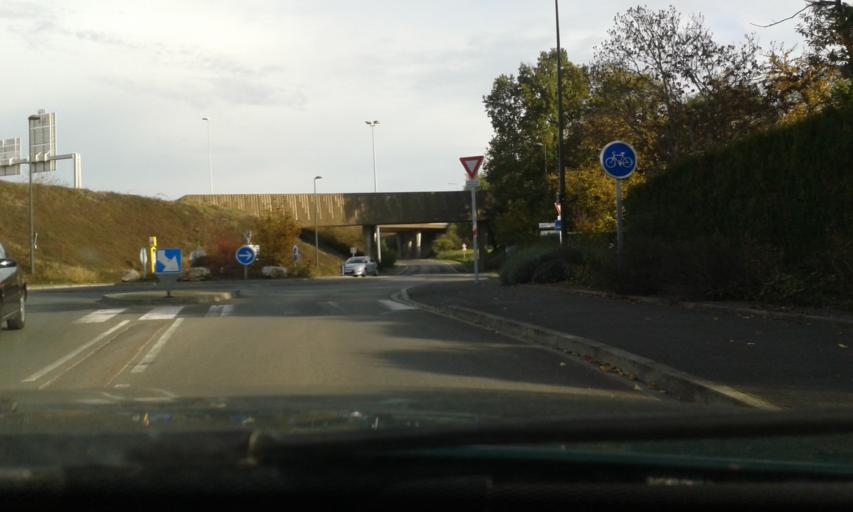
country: FR
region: Centre
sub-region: Departement du Loiret
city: Olivet
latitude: 47.8454
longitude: 1.9089
